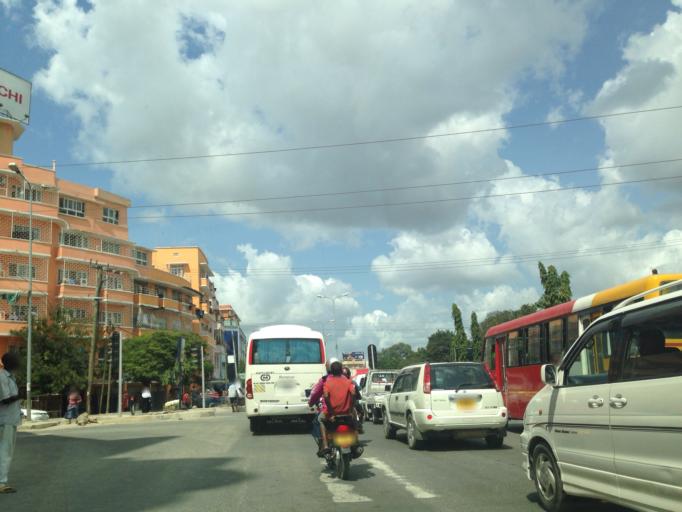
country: TZ
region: Dar es Salaam
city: Dar es Salaam
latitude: -6.8212
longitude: 39.2813
